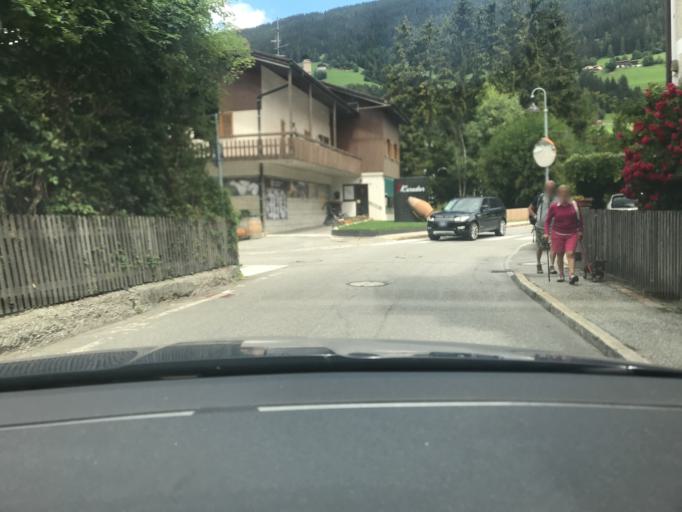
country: IT
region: Trentino-Alto Adige
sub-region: Bolzano
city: San Candido
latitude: 46.7324
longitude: 12.2761
